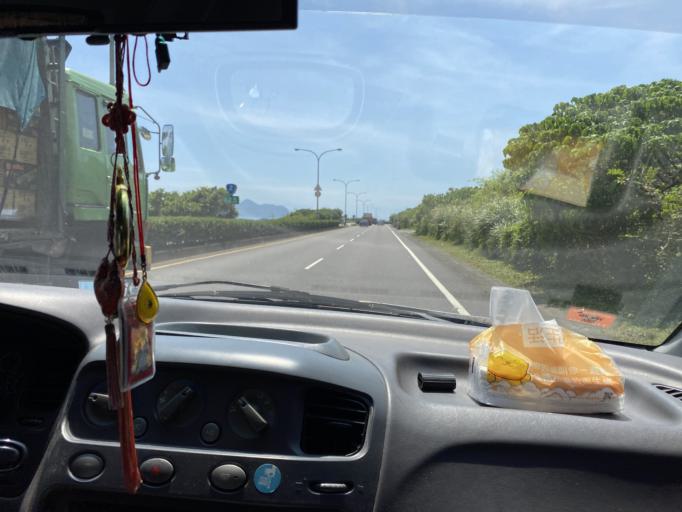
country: TW
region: Taiwan
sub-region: Yilan
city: Yilan
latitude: 24.9302
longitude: 121.8850
